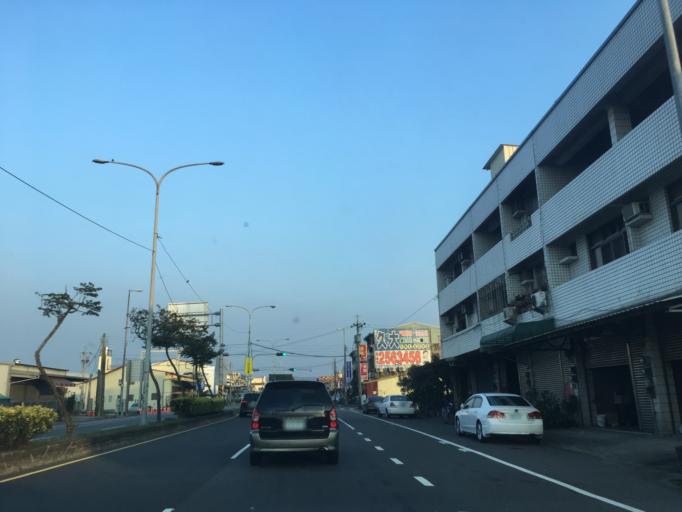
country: TW
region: Taiwan
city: Zhongxing New Village
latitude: 24.0036
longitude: 120.6545
